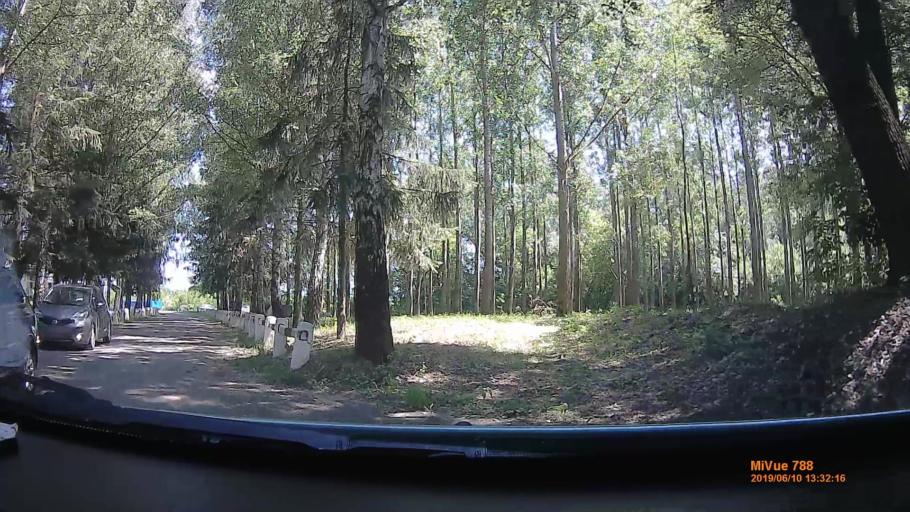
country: HU
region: Szabolcs-Szatmar-Bereg
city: Tiszadob
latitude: 48.0094
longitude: 21.1424
